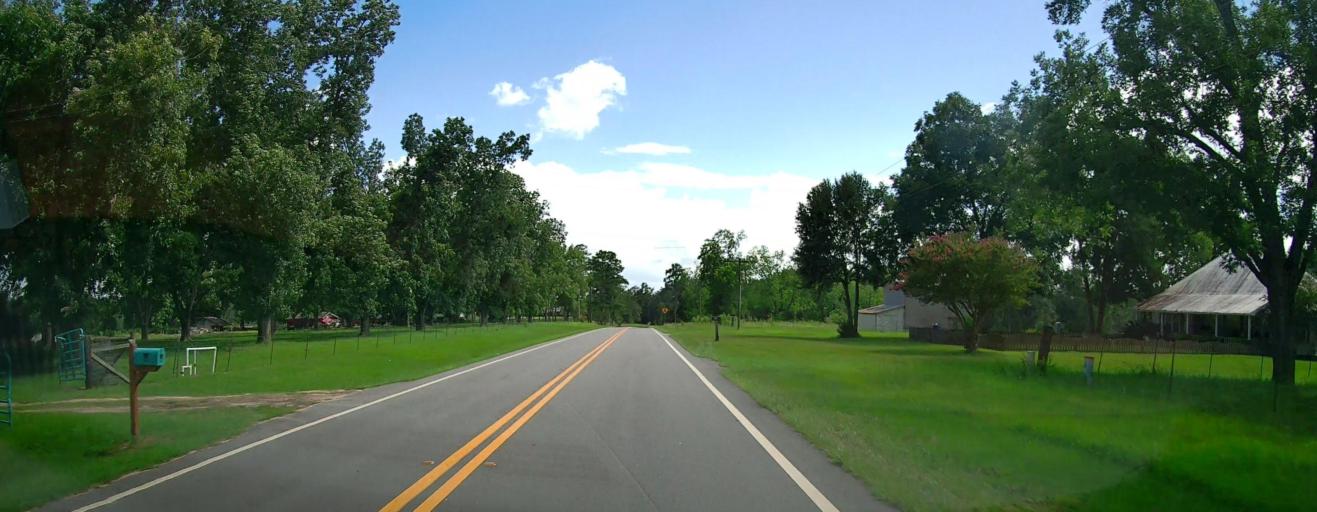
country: US
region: Georgia
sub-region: Irwin County
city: Ocilla
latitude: 31.5990
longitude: -83.1652
